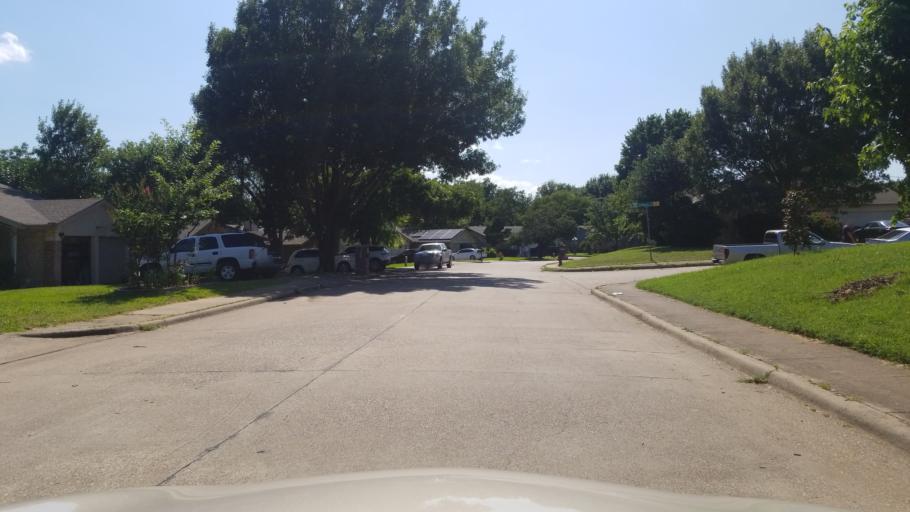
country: US
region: Texas
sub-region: Dallas County
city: Grand Prairie
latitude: 32.6771
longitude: -97.0129
